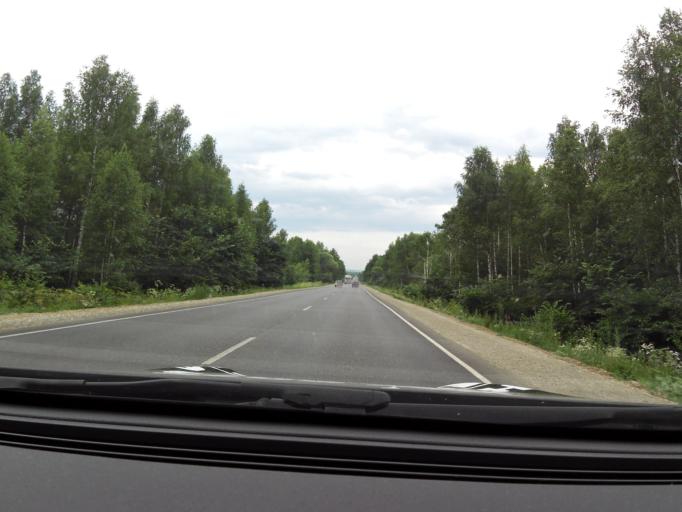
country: RU
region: Bashkortostan
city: Ulu-Telyak
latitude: 54.8368
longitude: 57.0186
